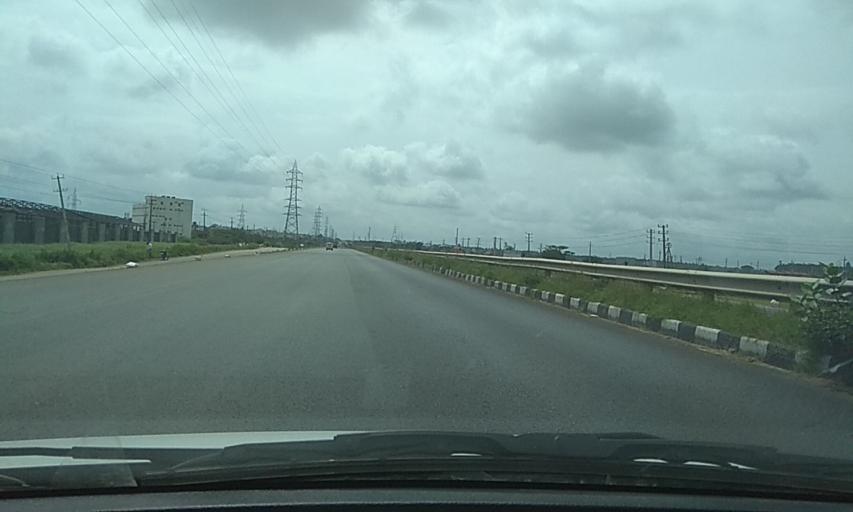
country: IN
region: Karnataka
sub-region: Davanagere
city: Harihar
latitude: 14.4392
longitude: 75.9043
